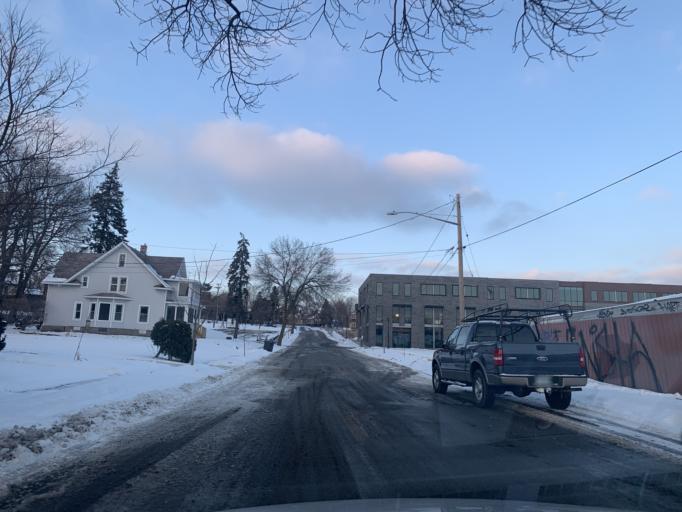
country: US
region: Minnesota
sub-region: Hennepin County
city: Minneapolis
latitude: 44.9772
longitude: -93.3007
